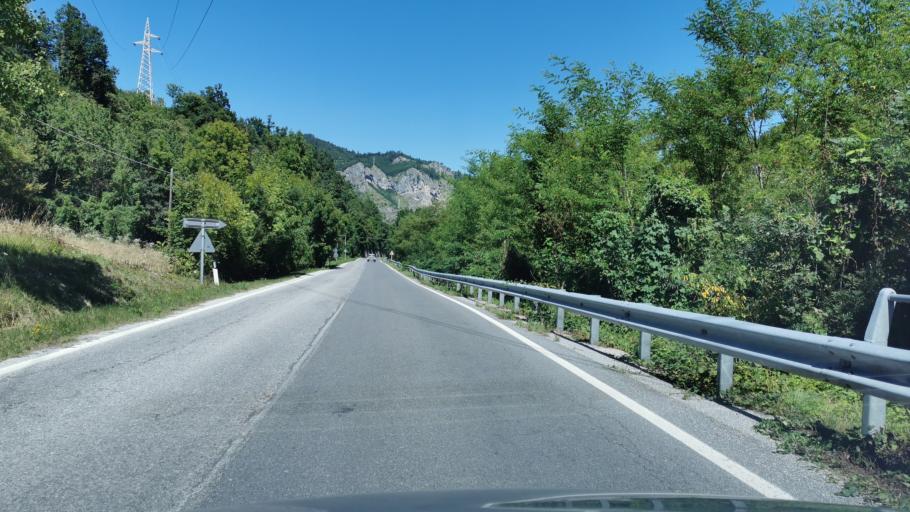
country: IT
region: Piedmont
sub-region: Provincia di Cuneo
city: Valdieri
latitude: 44.2862
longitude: 7.4170
